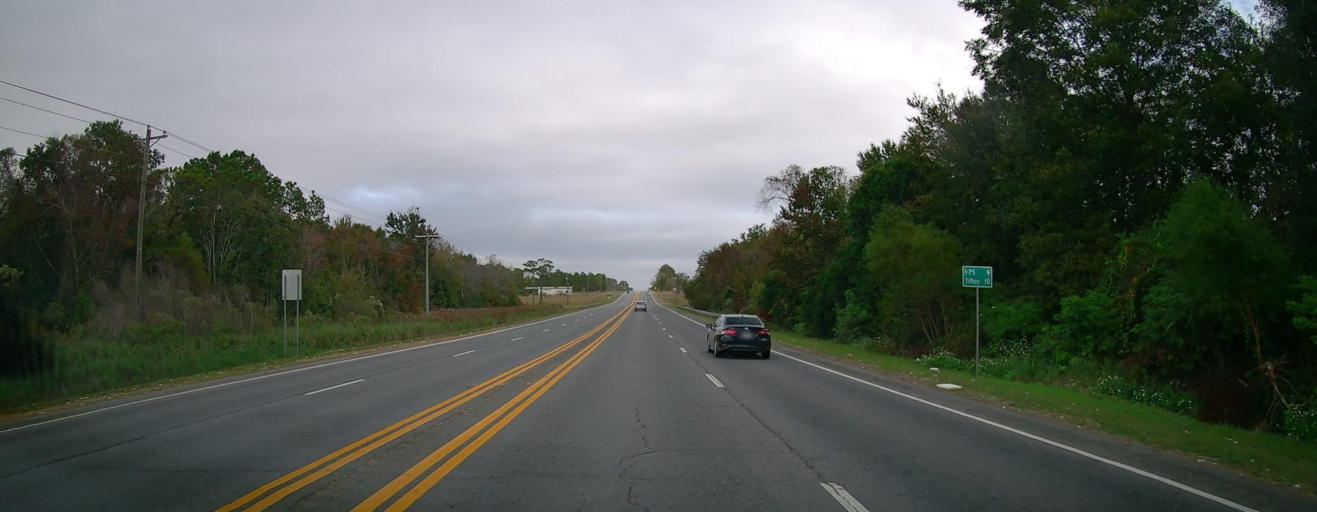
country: US
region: Georgia
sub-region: Tift County
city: Omega
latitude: 31.3494
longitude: -83.5865
